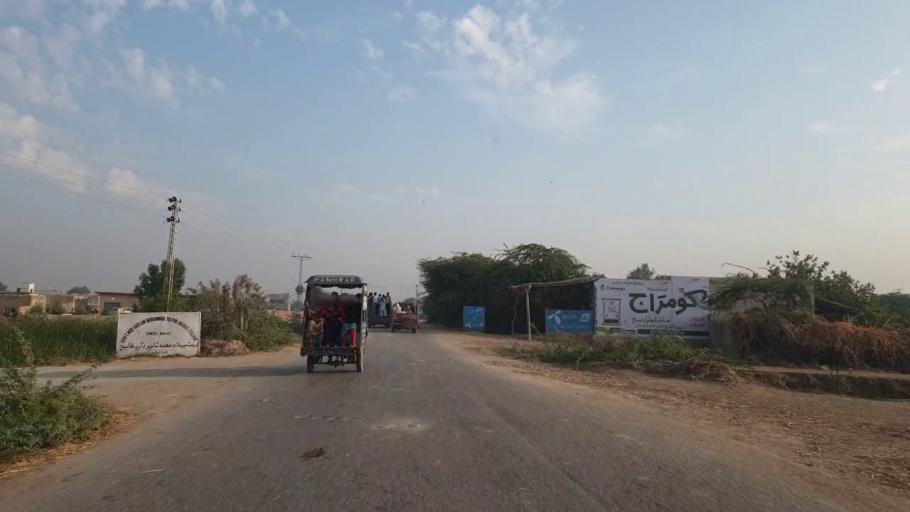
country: PK
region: Sindh
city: Tando Bago
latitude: 24.7759
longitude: 68.9608
